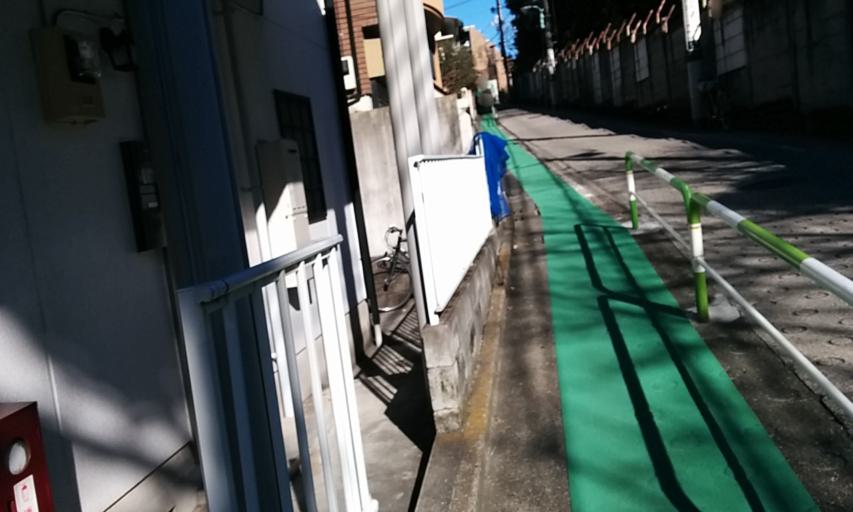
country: JP
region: Tokyo
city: Tokyo
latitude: 35.7214
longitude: 139.7408
